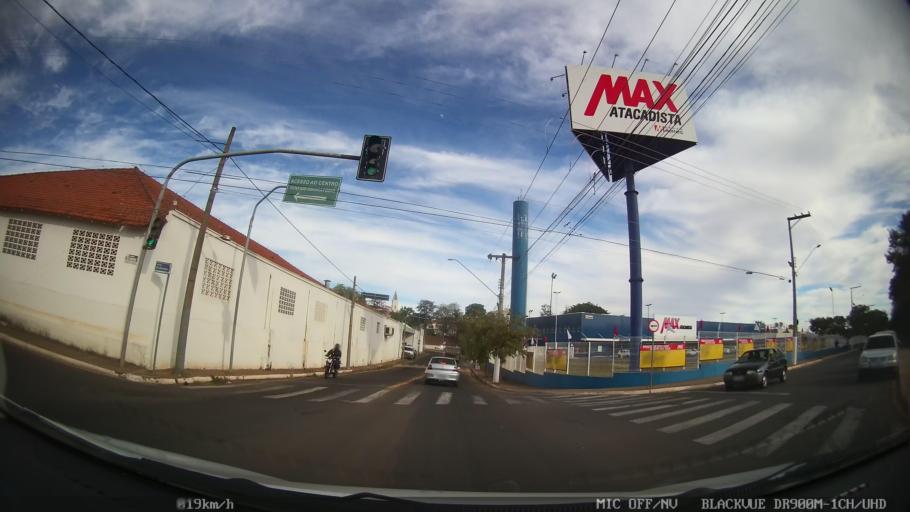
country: BR
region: Sao Paulo
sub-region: Catanduva
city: Catanduva
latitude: -21.1287
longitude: -48.9799
